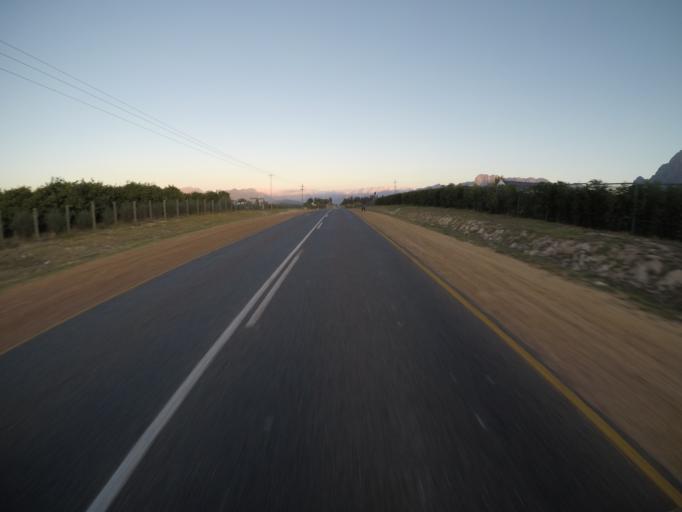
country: ZA
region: Western Cape
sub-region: Cape Winelands District Municipality
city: Paarl
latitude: -33.8255
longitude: 18.9356
